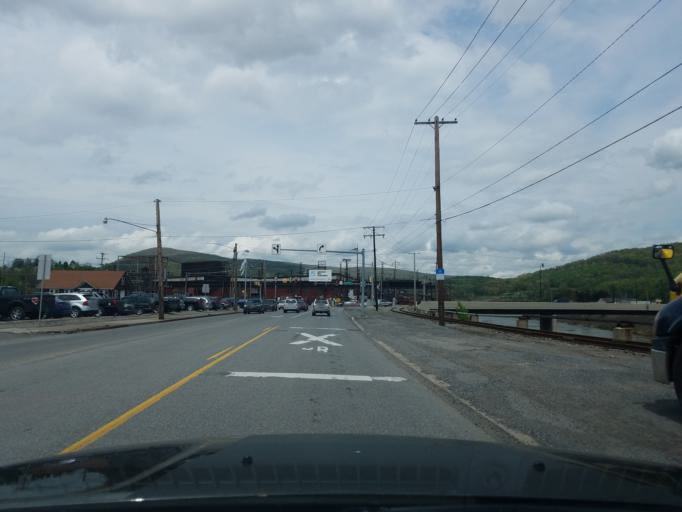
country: US
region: Pennsylvania
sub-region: Cambria County
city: Johnstown
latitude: 40.3483
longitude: -78.9409
